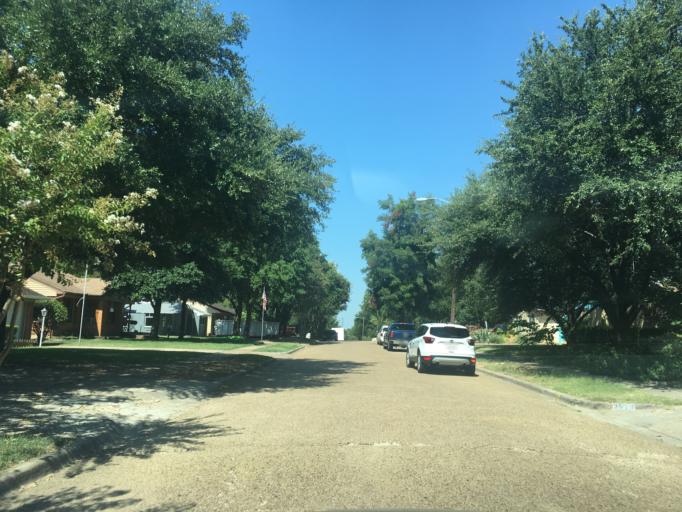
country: US
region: Texas
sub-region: Dallas County
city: Garland
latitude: 32.8533
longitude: -96.6697
